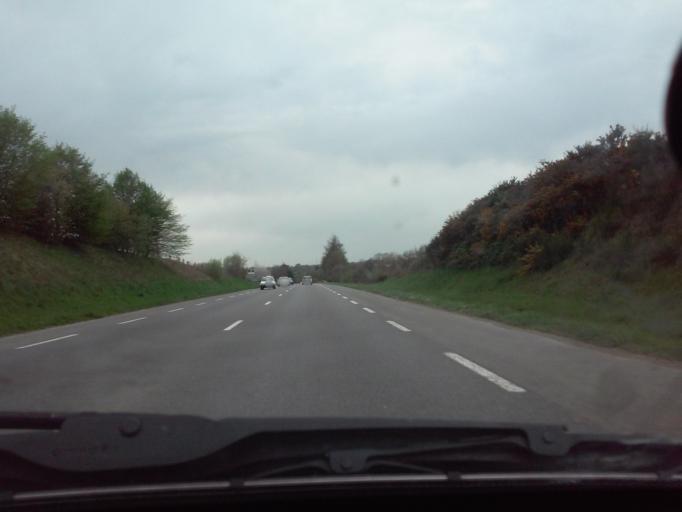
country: FR
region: Brittany
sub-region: Departement d'Ille-et-Vilaine
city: Fougeres
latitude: 48.3368
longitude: -1.1994
